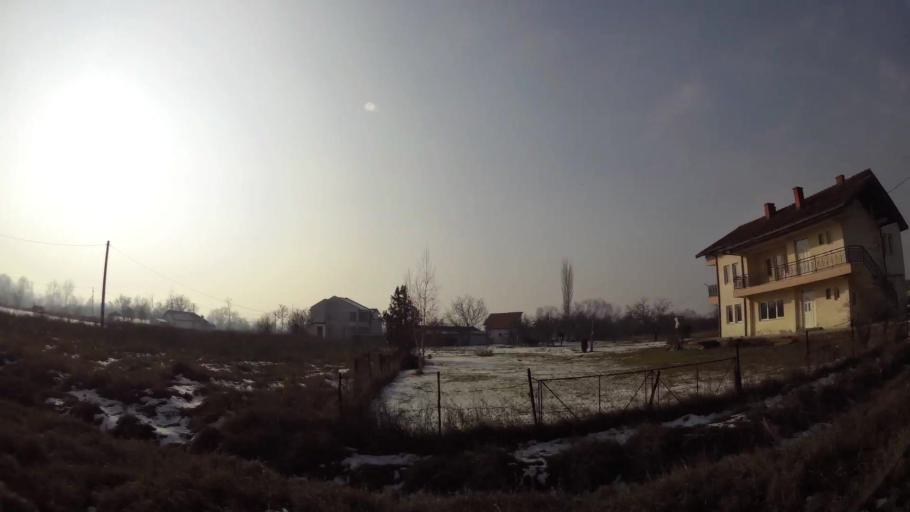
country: MK
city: Kadino
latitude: 41.9706
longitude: 21.5934
